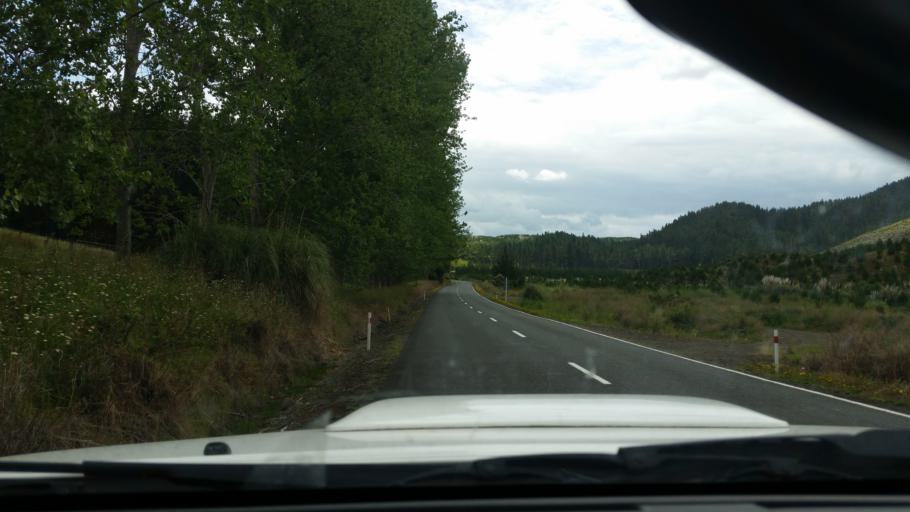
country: NZ
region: Northland
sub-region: Kaipara District
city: Dargaville
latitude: -35.7409
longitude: 173.8752
